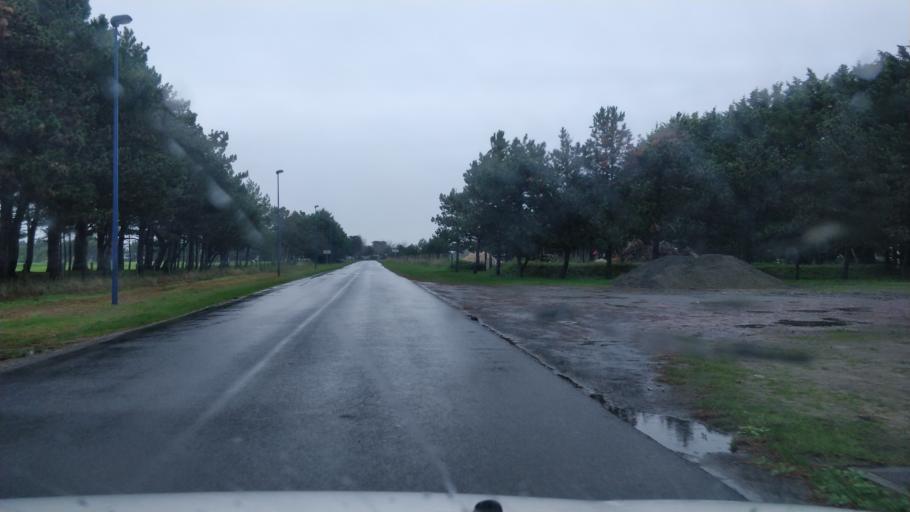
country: FR
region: Lower Normandy
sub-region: Departement de la Manche
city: Brehal
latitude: 48.9049
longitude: -1.5643
